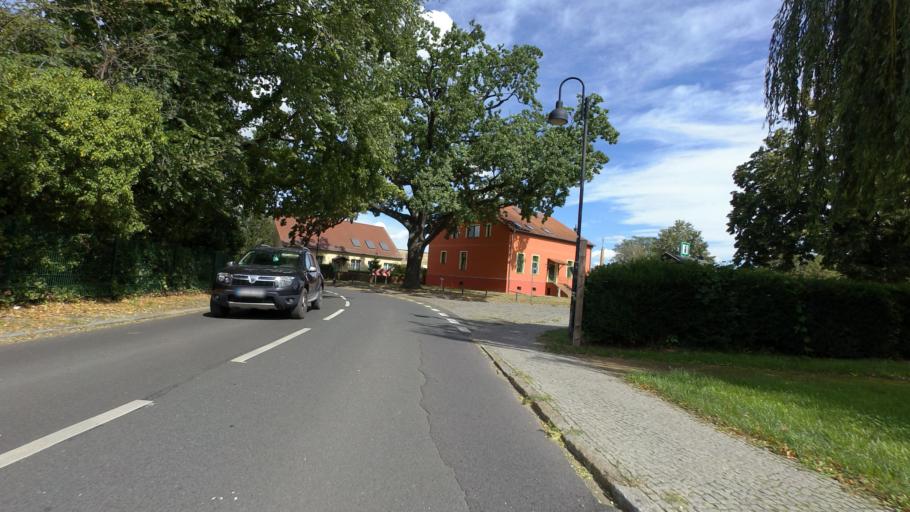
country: DE
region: Brandenburg
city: Gross Kreutz
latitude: 52.4053
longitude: 12.7767
